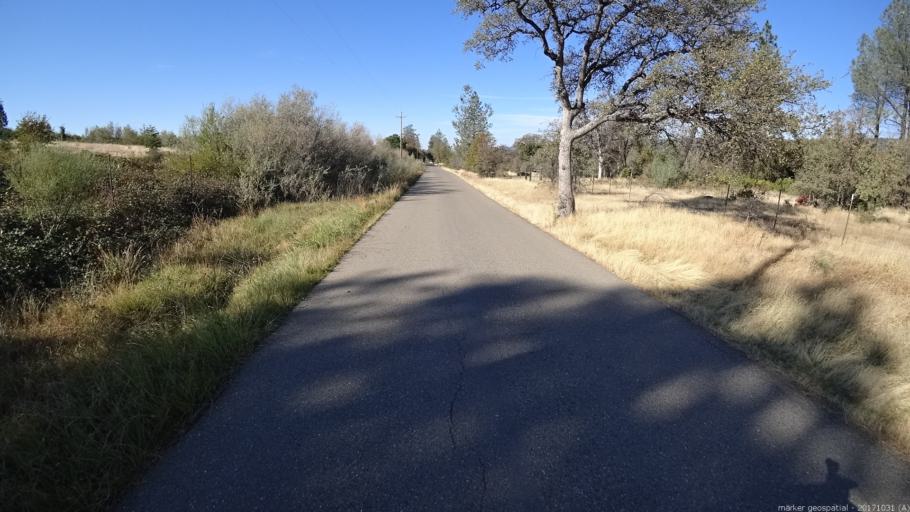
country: US
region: California
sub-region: Shasta County
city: Shingletown
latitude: 40.4462
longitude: -121.8428
